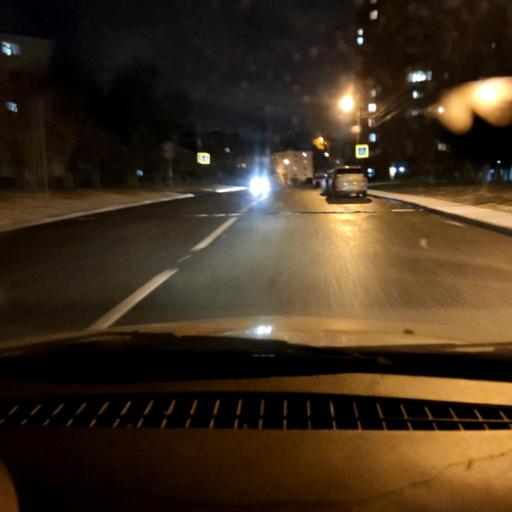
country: RU
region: Bashkortostan
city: Ufa
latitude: 54.7699
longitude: 56.0274
